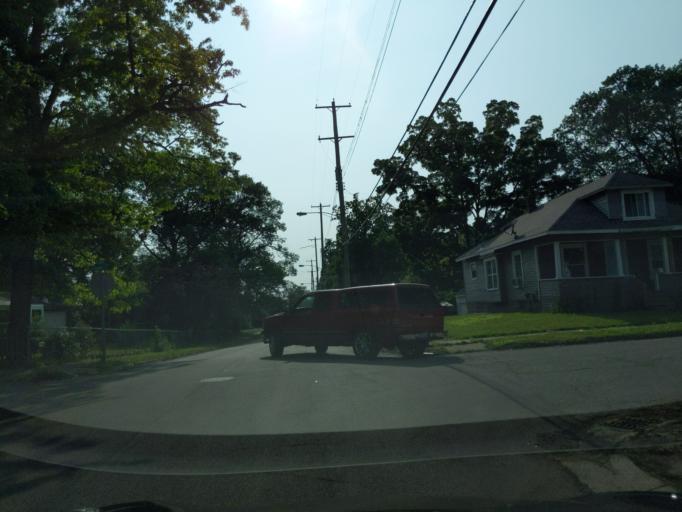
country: US
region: Michigan
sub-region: Ingham County
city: Lansing
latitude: 42.7210
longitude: -84.5307
